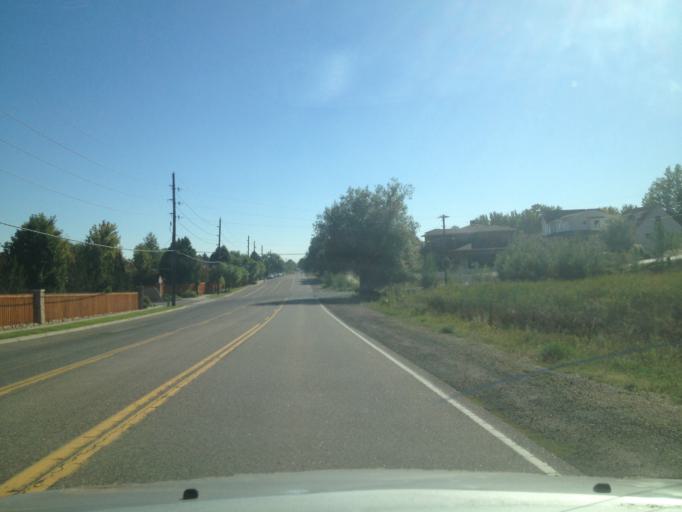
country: US
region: Colorado
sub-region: Jefferson County
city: Applewood
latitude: 39.7617
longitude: -105.1665
